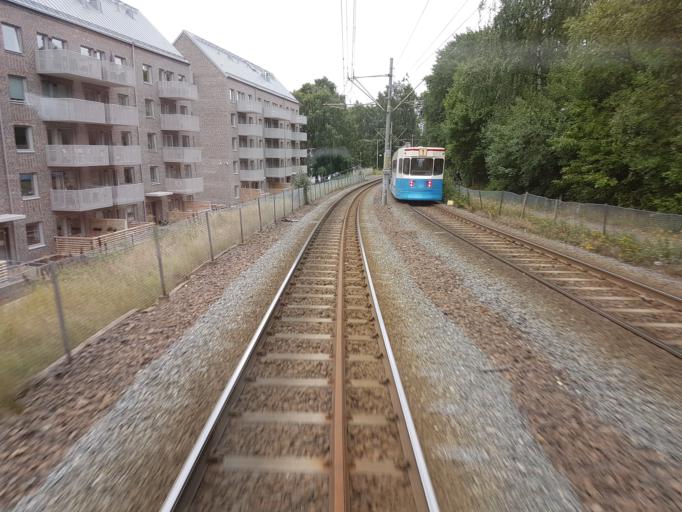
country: SE
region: Vaestra Goetaland
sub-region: Goteborg
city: Majorna
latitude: 57.6635
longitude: 11.9252
